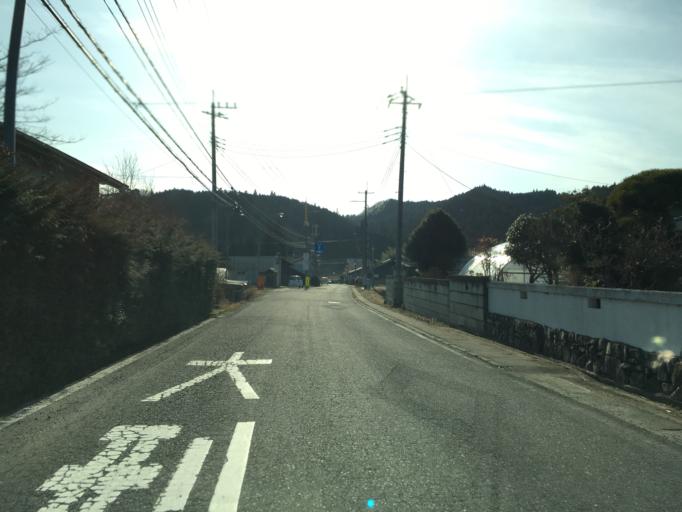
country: JP
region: Ibaraki
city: Daigo
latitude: 36.7153
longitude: 140.4989
